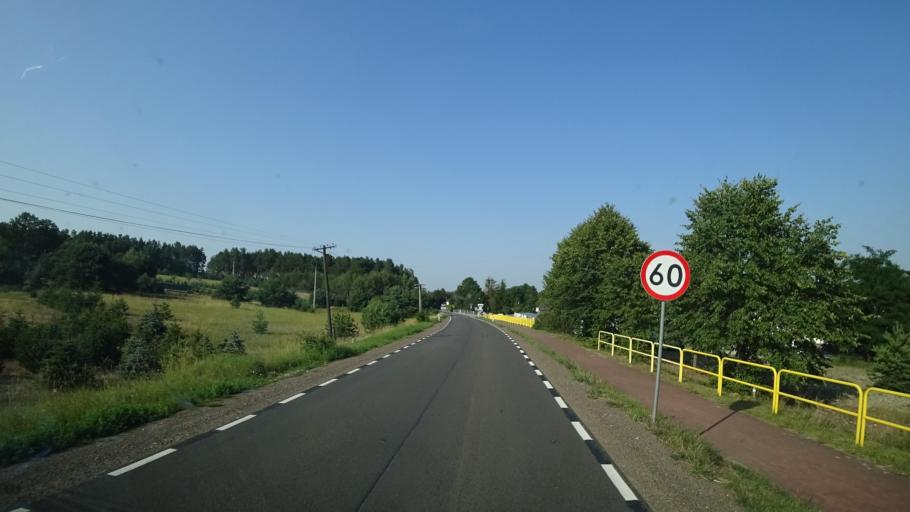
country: PL
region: Pomeranian Voivodeship
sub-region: Powiat bytowski
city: Lipnica
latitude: 53.8551
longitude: 17.4908
